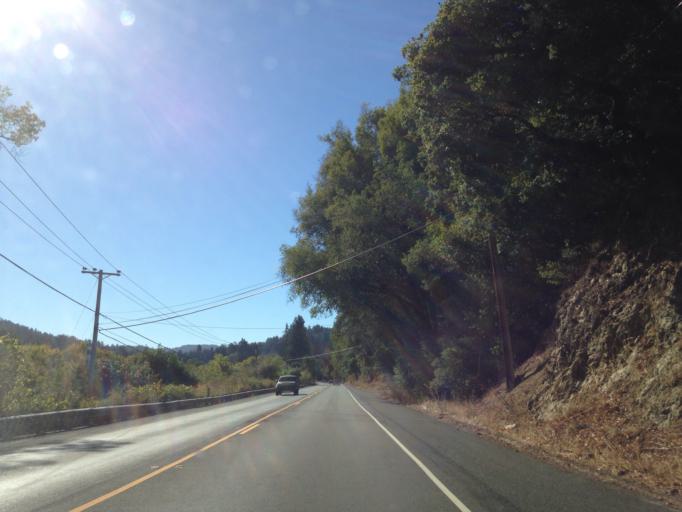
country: US
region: California
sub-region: Sonoma County
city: Guerneville
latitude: 38.5063
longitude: -122.9514
